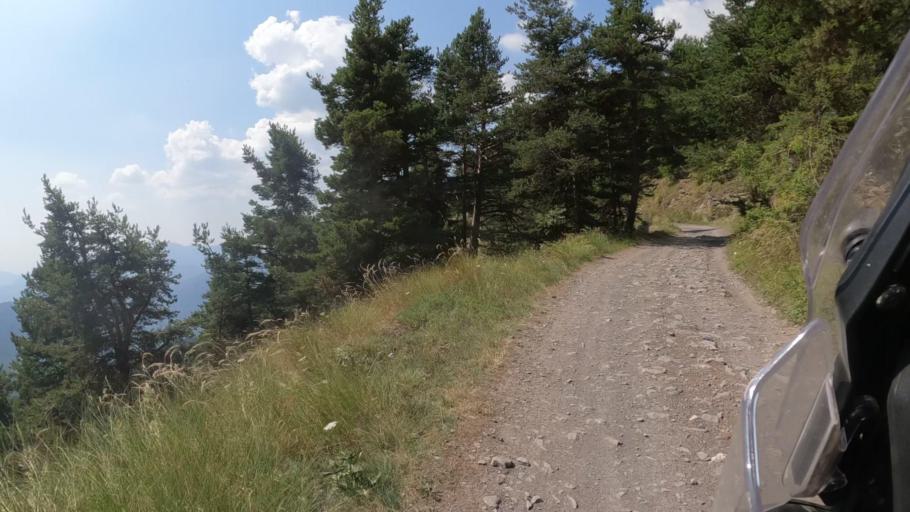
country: IT
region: Piedmont
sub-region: Provincia di Cuneo
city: Briga Alta
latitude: 44.0385
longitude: 7.6970
